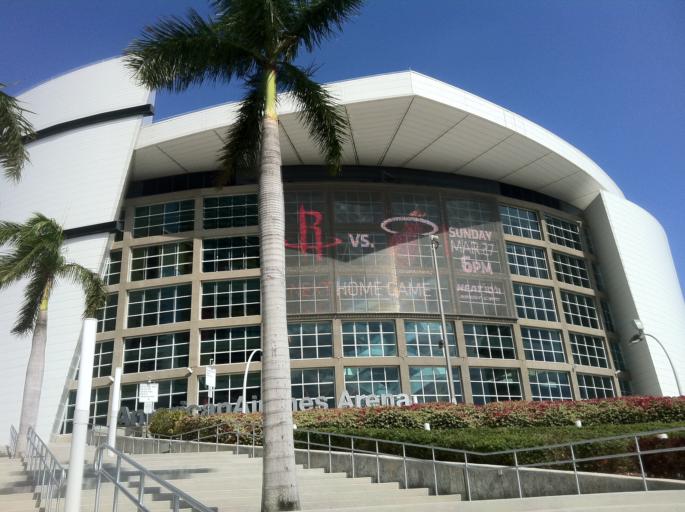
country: US
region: Florida
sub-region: Miami-Dade County
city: Miami
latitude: 25.7812
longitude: -80.1888
